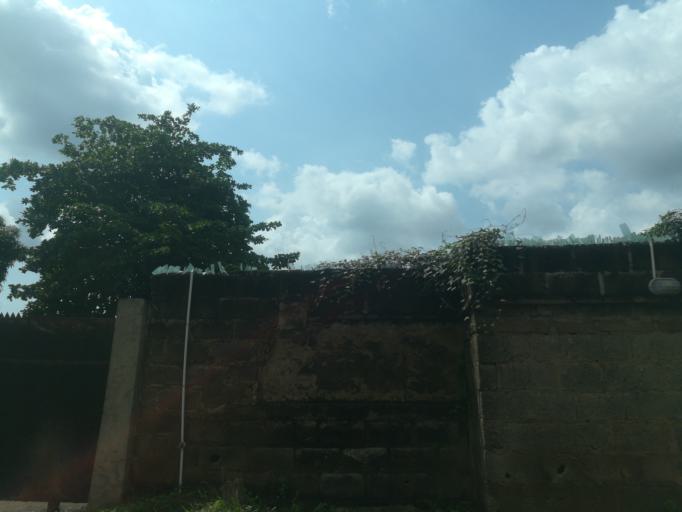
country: NG
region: Oyo
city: Ibadan
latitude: 7.3621
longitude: 3.8524
